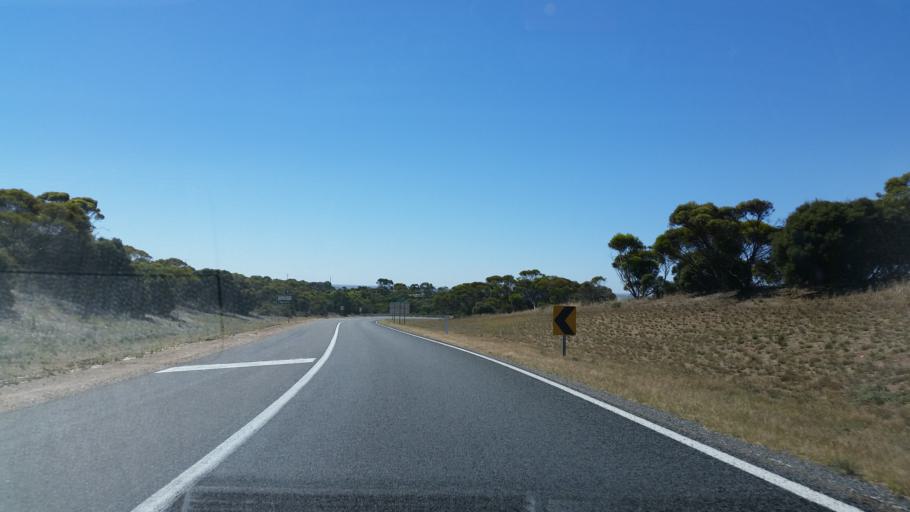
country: AU
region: South Australia
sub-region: Murray Bridge
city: Murray Bridge
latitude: -35.1431
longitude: 139.2269
